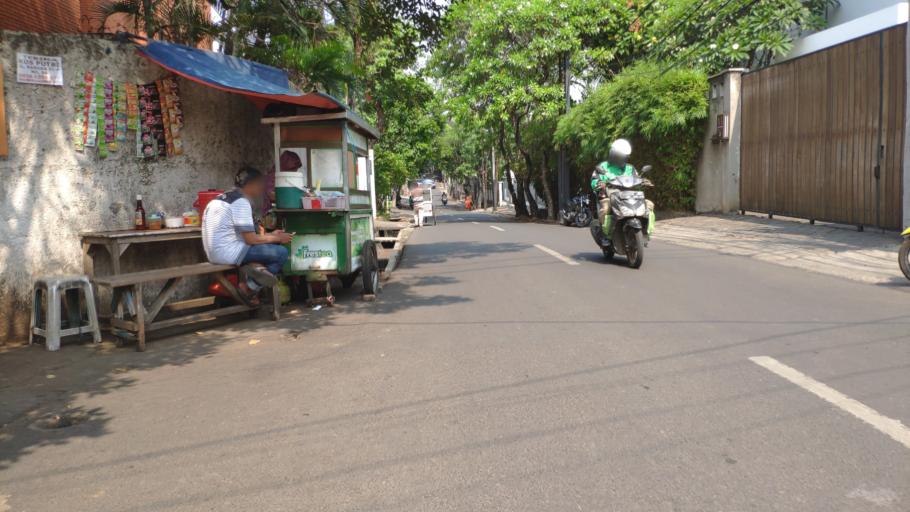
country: ID
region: Jakarta Raya
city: Jakarta
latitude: -6.2546
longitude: 106.8156
